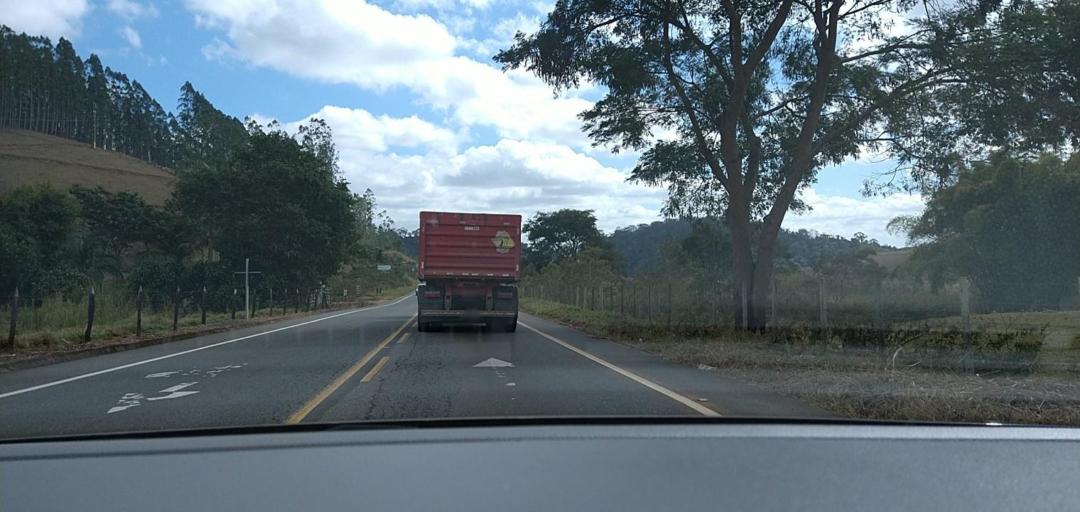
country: BR
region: Minas Gerais
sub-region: Ponte Nova
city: Ponte Nova
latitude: -20.4809
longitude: -42.8801
